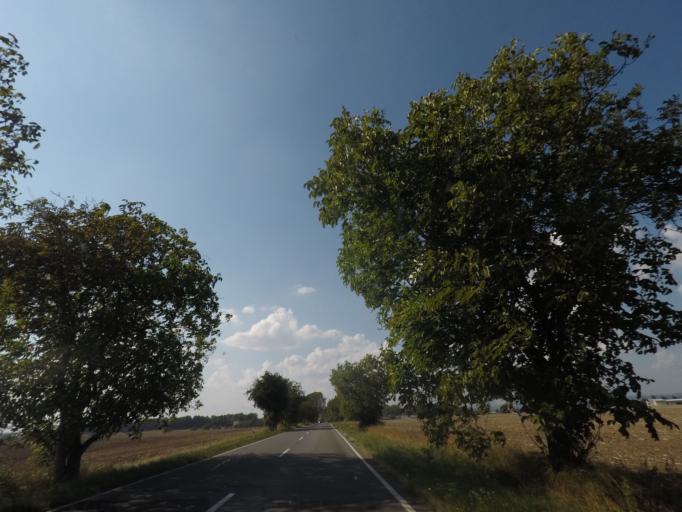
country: CZ
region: Kralovehradecky
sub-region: Okres Nachod
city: Jaromer
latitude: 50.3305
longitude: 15.9429
